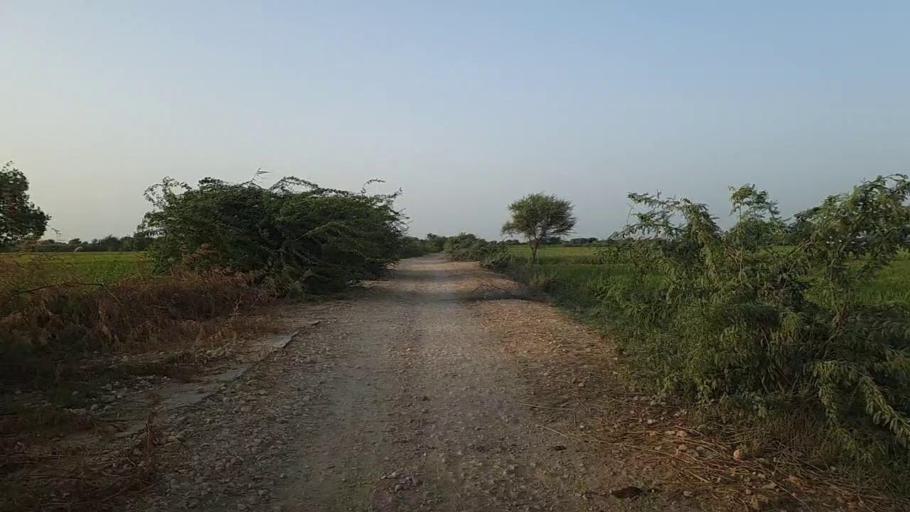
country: PK
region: Sindh
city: Kario
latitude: 24.7108
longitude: 68.4620
